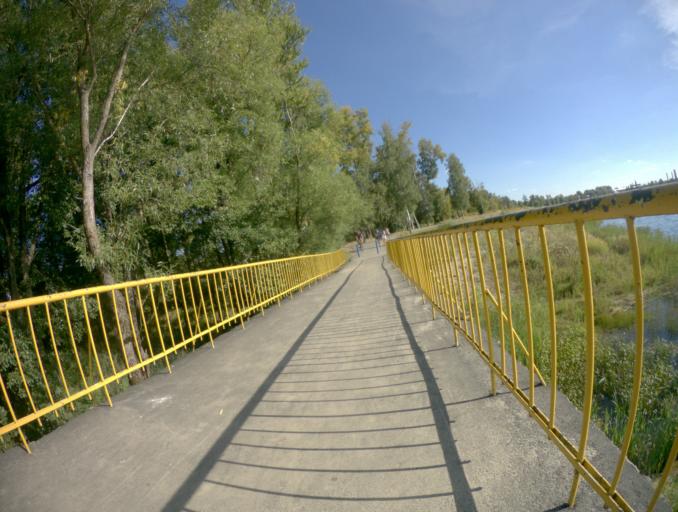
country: RU
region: Vladimir
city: Gus'-Khrustal'nyy
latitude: 55.6249
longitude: 40.6721
